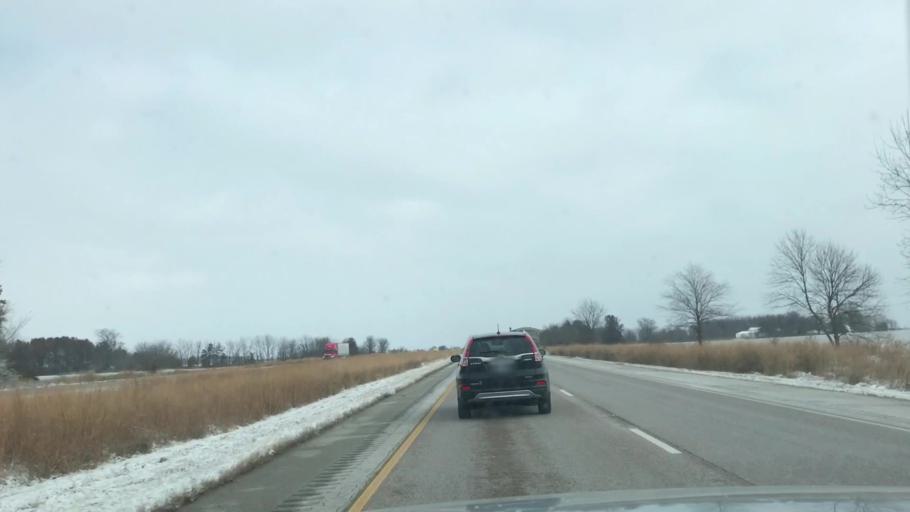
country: US
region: Illinois
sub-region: Macoupin County
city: Mount Olive
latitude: 39.1280
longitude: -89.7143
